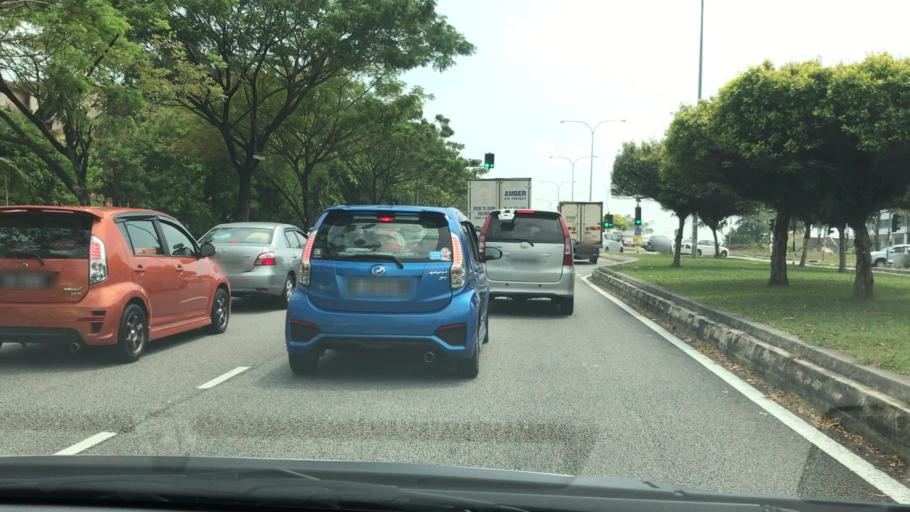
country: MY
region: Putrajaya
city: Putrajaya
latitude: 2.9979
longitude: 101.6649
